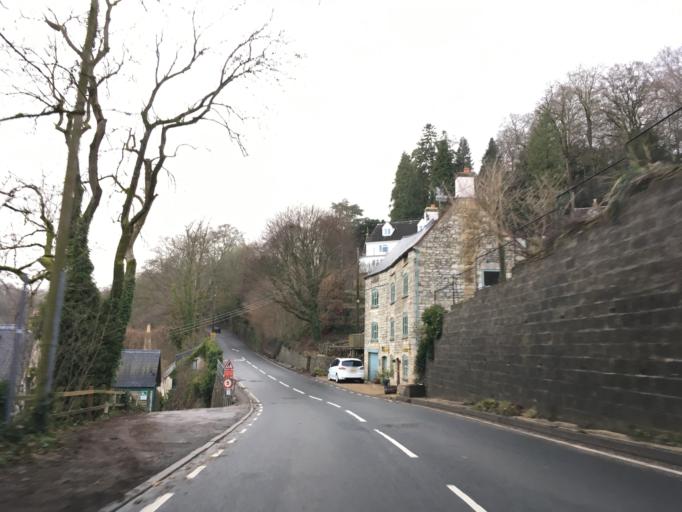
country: GB
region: England
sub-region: Gloucestershire
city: Nailsworth
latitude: 51.6872
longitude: -2.2264
